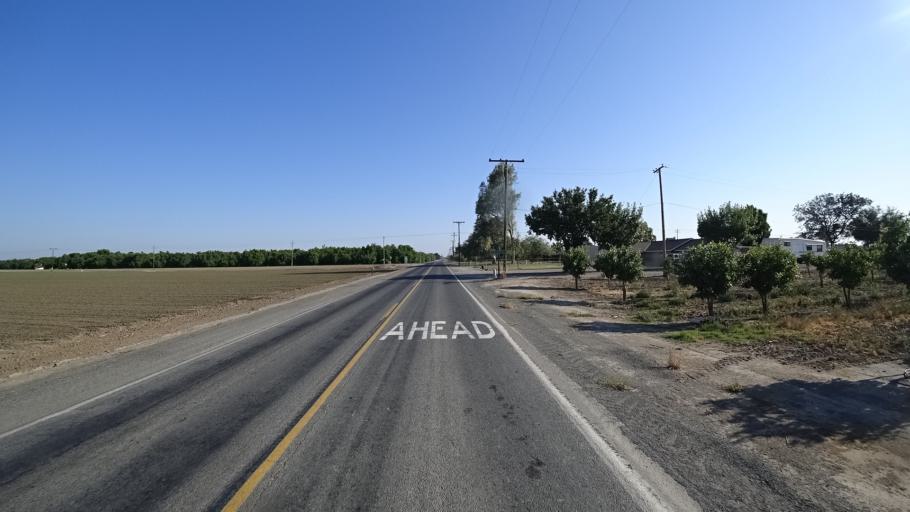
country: US
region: California
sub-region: Kings County
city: Armona
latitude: 36.2969
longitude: -119.7093
